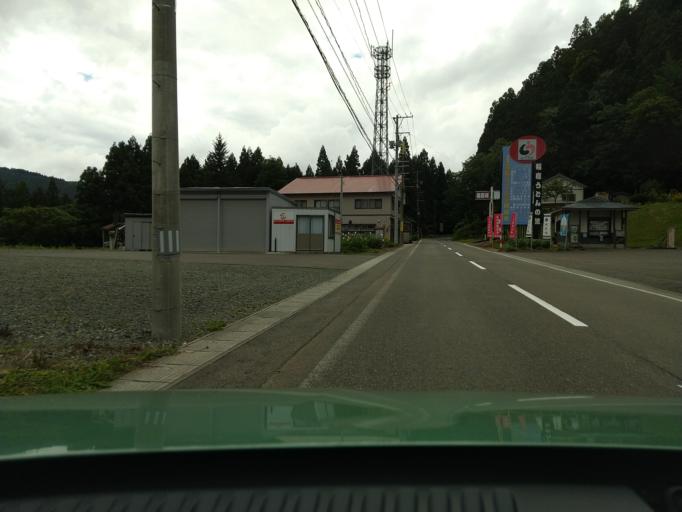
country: JP
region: Akita
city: Yuzawa
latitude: 39.0927
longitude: 140.5804
